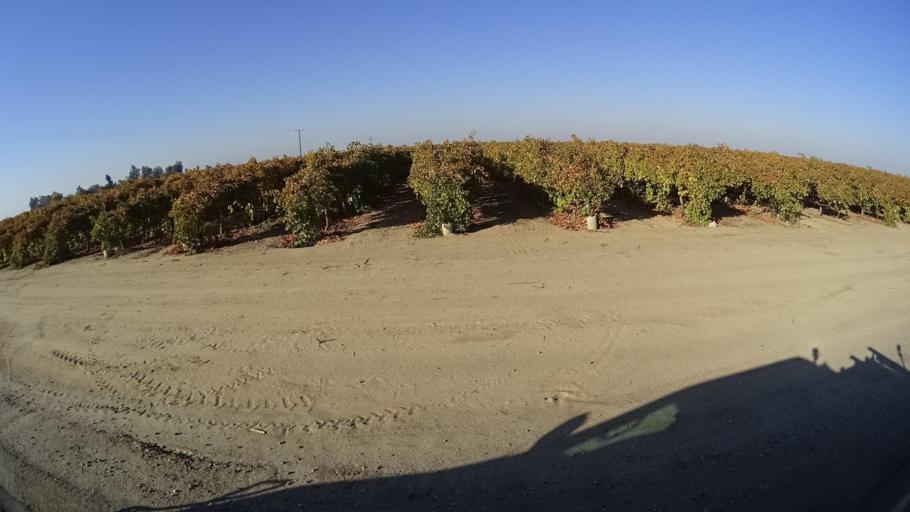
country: US
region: California
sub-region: Tulare County
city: Richgrove
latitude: 35.7511
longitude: -119.1696
